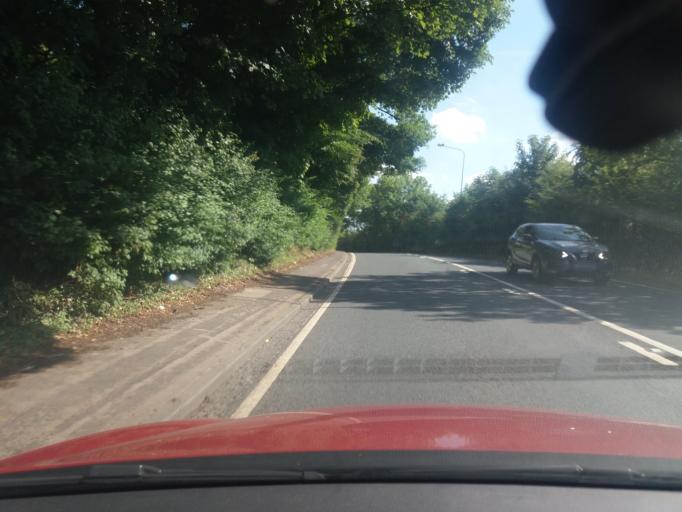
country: GB
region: England
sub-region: Lancashire
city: Adlington
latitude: 53.6255
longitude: -2.6199
